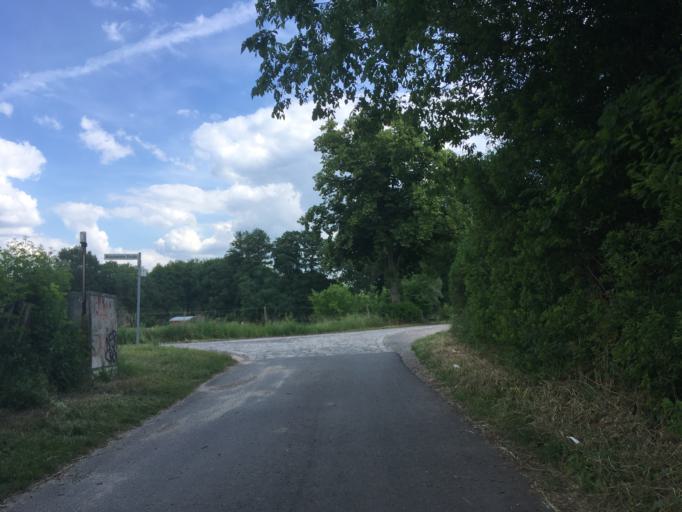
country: DE
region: Brandenburg
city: Waldsieversdorf
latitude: 52.5298
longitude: 14.1017
